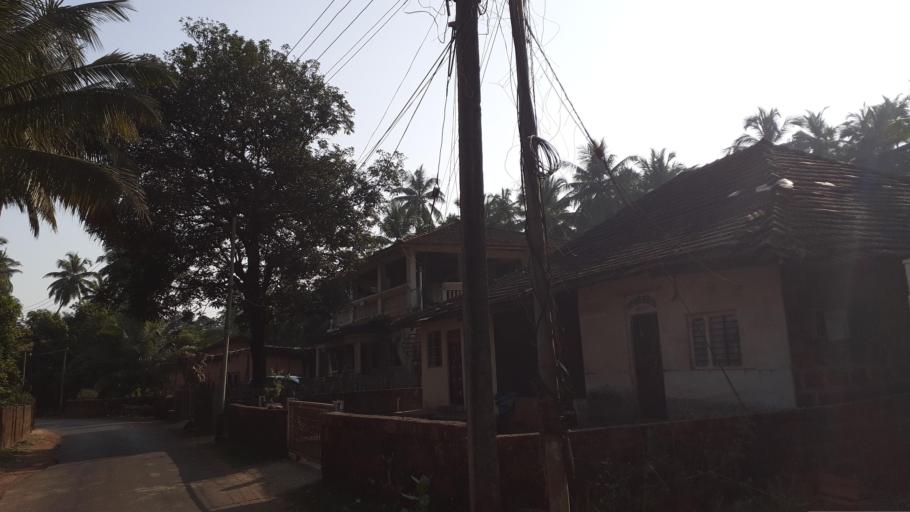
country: IN
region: Maharashtra
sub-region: Ratnagiri
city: Ratnagiri
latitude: 17.2164
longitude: 73.2477
